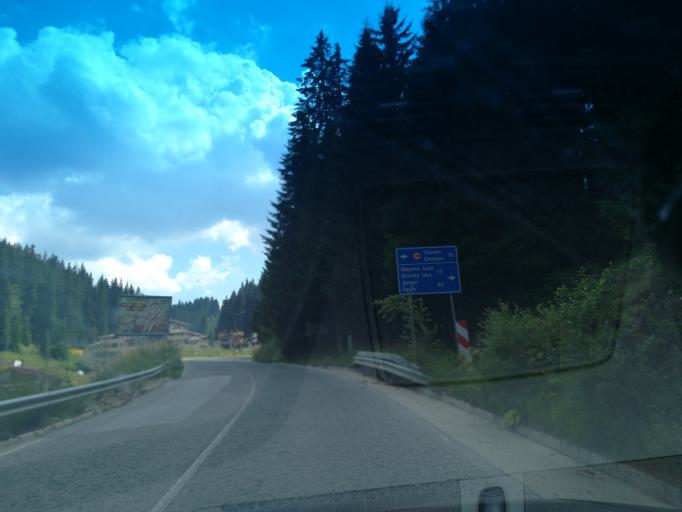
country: BG
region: Smolyan
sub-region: Obshtina Smolyan
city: Smolyan
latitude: 41.6527
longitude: 24.6960
